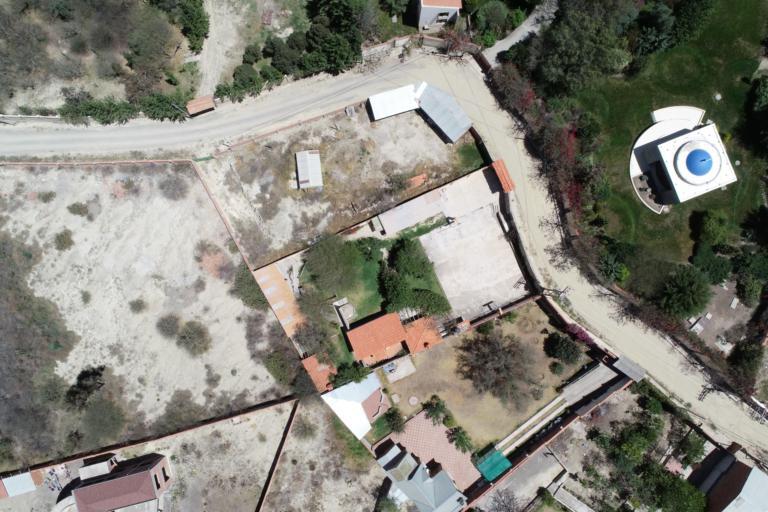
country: BO
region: La Paz
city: La Paz
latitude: -16.6445
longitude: -68.0450
